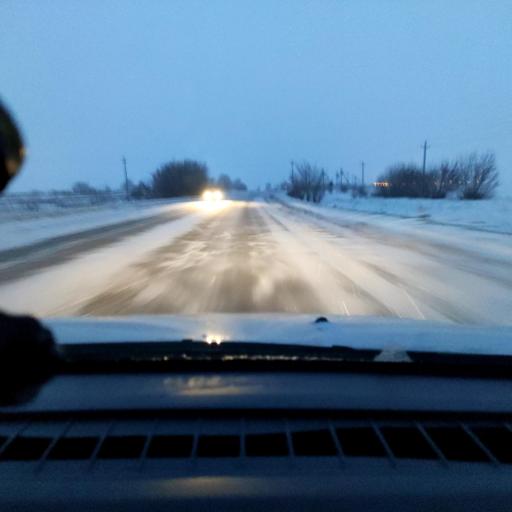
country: RU
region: Samara
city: Kinel'-Cherkassy
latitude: 53.4484
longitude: 51.5299
